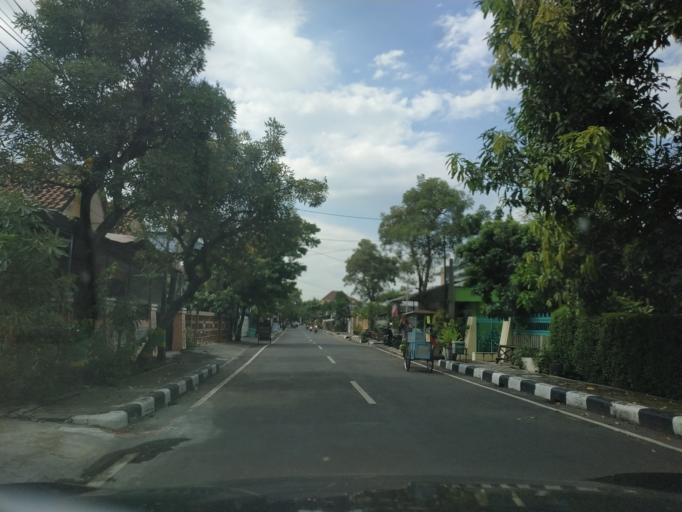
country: ID
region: Central Java
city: Pati
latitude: -6.7562
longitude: 111.0326
